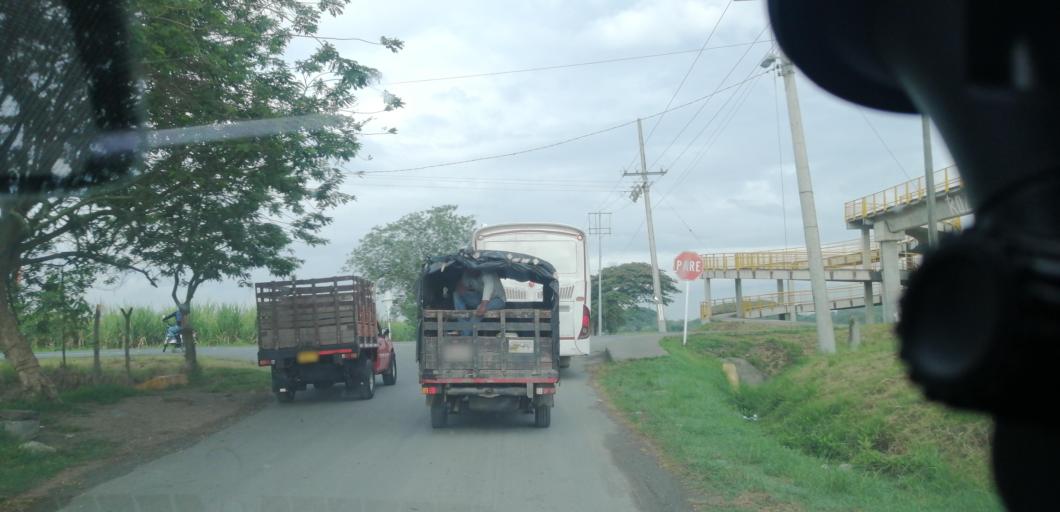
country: CO
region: Valle del Cauca
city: Yumbo
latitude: 3.5754
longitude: -76.4077
